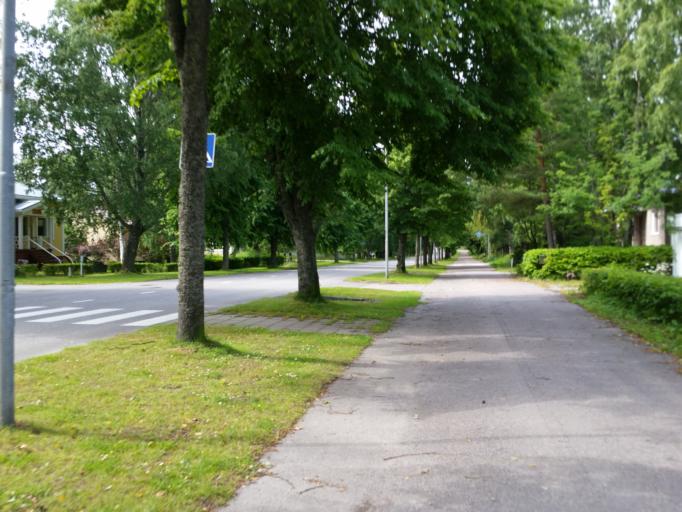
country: FI
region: Uusimaa
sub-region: Raaseporin
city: Hanko
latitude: 59.8274
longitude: 22.9378
